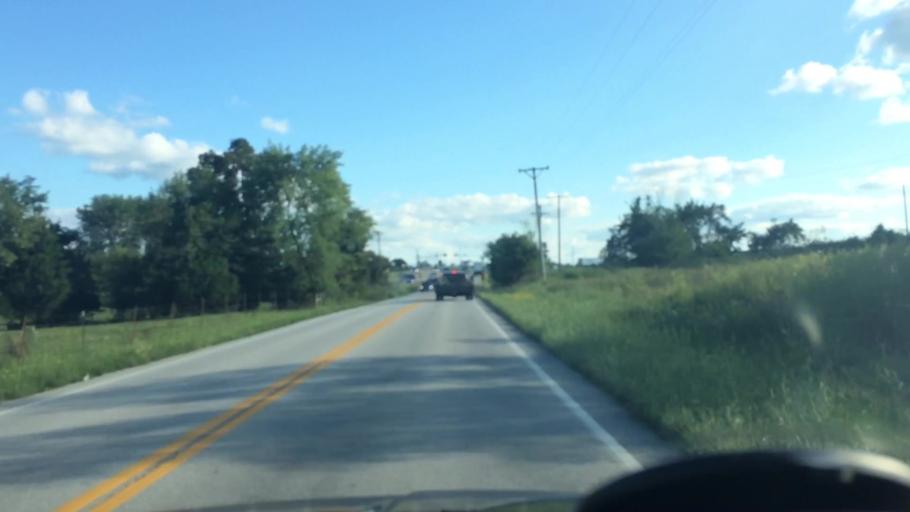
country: US
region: Missouri
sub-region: Greene County
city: Strafford
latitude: 37.2786
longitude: -93.1133
